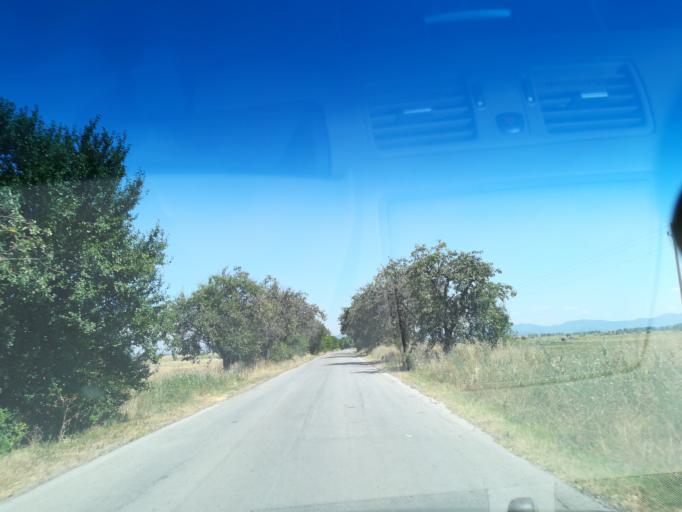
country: BG
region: Plovdiv
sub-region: Obshtina Sadovo
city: Sadovo
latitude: 42.0204
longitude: 25.0223
